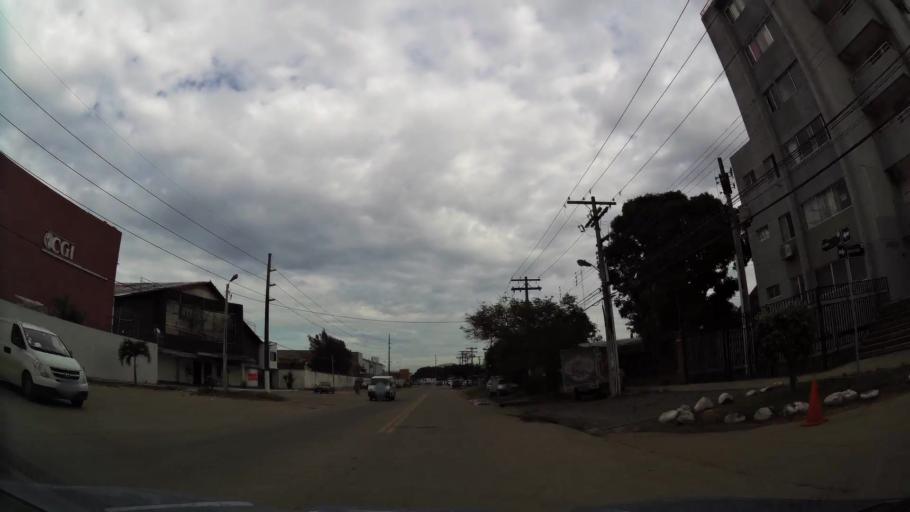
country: BO
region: Santa Cruz
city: Santa Cruz de la Sierra
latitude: -17.7579
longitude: -63.1754
